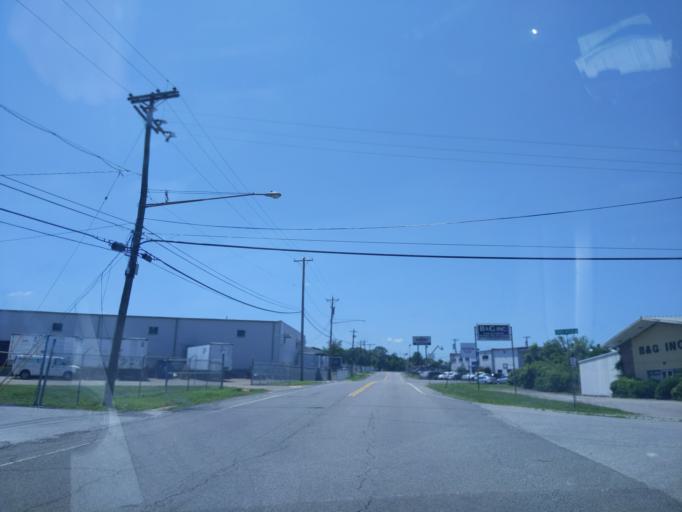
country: US
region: Tennessee
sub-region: Davidson County
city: Nashville
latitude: 36.1395
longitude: -86.7432
